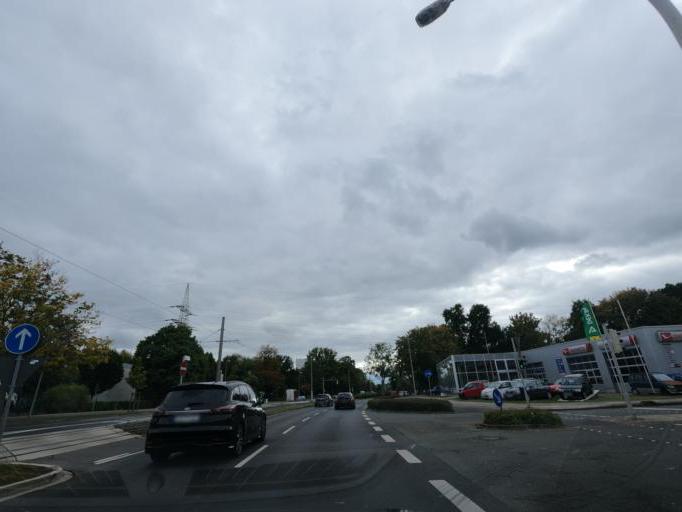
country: DE
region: Lower Saxony
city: Braunschweig
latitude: 52.2447
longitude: 10.4894
